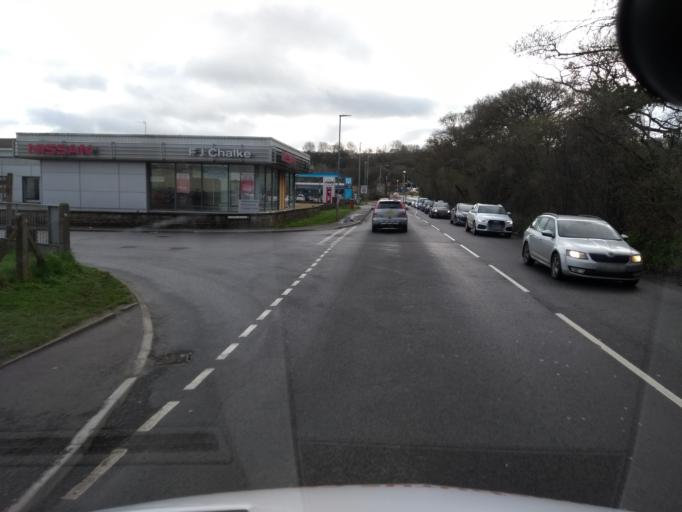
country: GB
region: England
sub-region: Somerset
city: Yeovil
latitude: 50.9426
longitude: -2.6110
